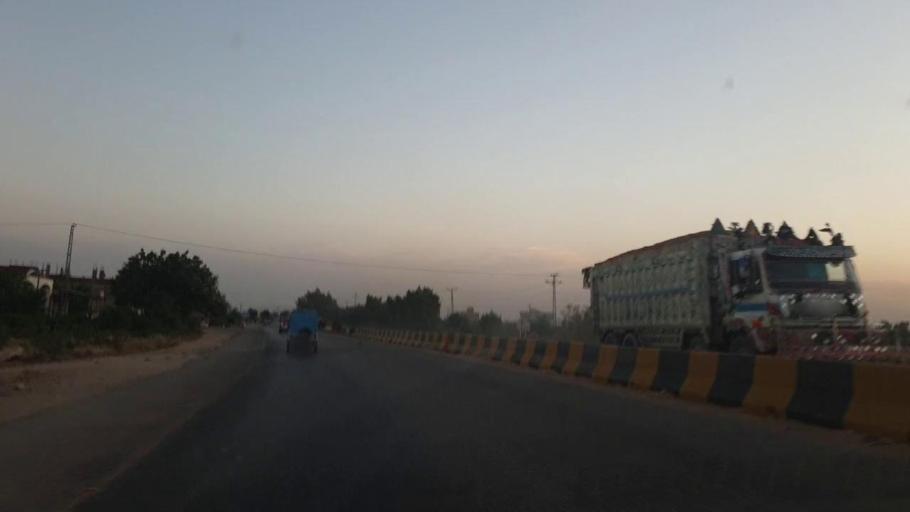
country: PK
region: Sindh
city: Kotri
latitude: 25.3909
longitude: 68.2732
